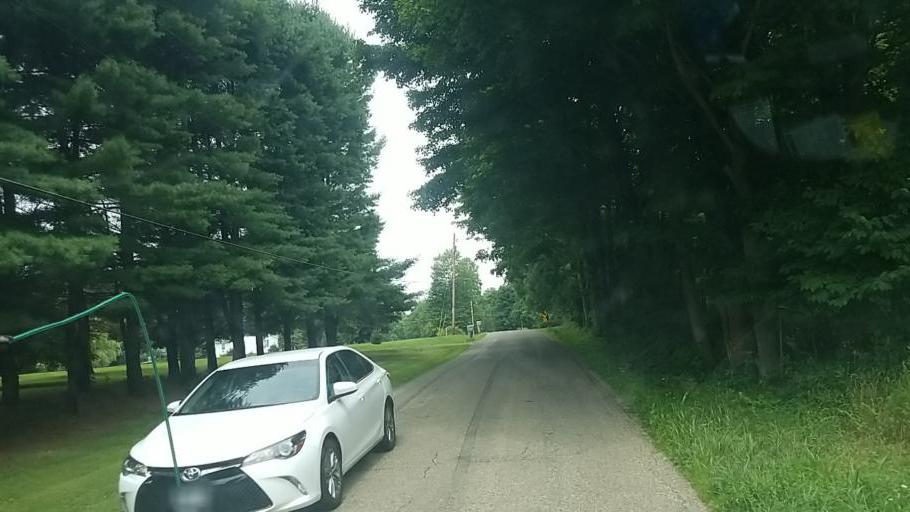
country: US
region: Ohio
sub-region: Richland County
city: Lexington
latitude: 40.6575
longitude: -82.6016
